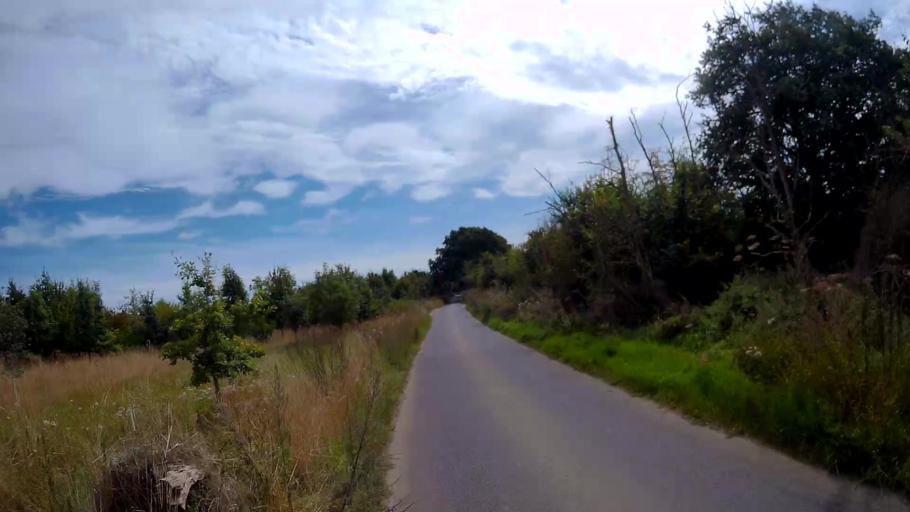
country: GB
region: England
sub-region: Hampshire
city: Odiham
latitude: 51.2327
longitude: -0.9630
